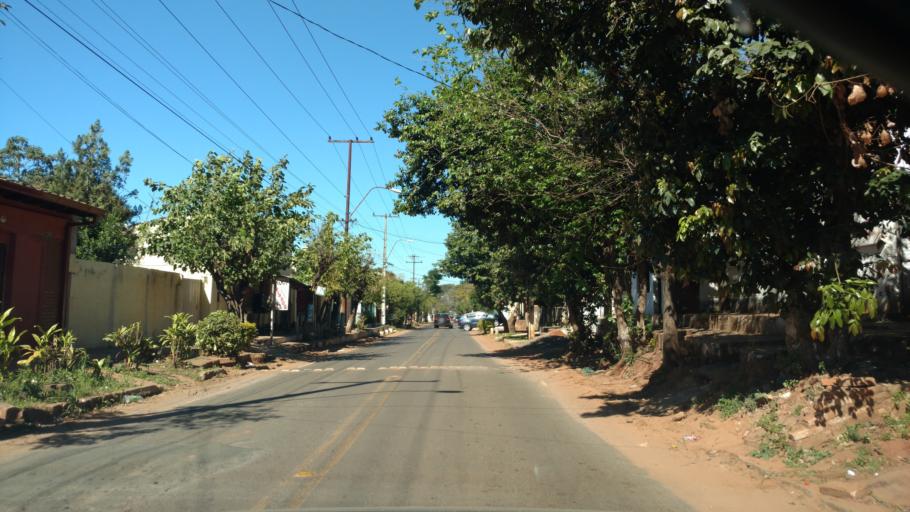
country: PY
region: Paraguari
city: Yaguaron
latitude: -25.5563
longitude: -57.2832
